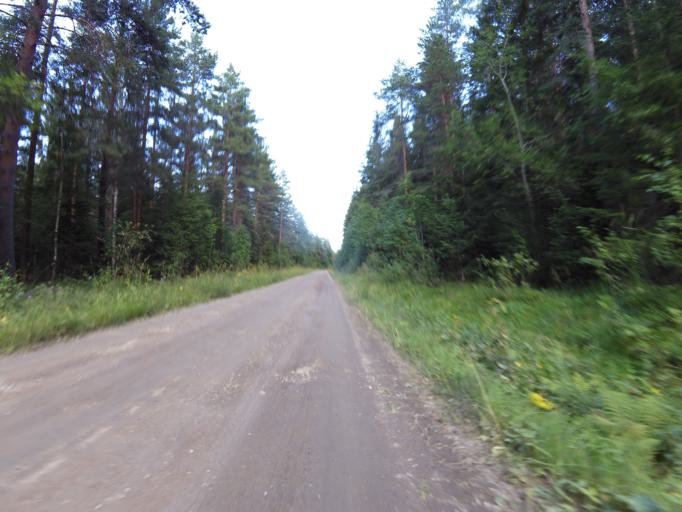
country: SE
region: Gaevleborg
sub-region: Hofors Kommun
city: Hofors
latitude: 60.5048
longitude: 16.3779
